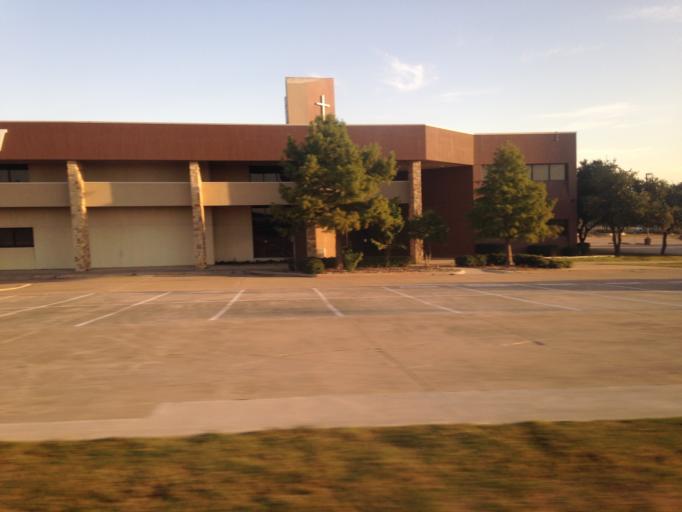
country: US
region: Texas
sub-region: Tarrant County
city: Watauga
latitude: 32.8402
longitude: -97.2782
